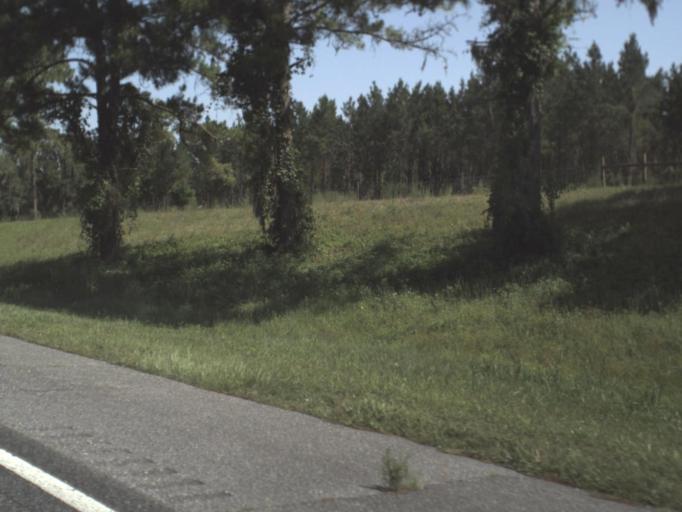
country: US
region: Florida
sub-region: Suwannee County
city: Live Oak
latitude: 30.3202
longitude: -82.9479
